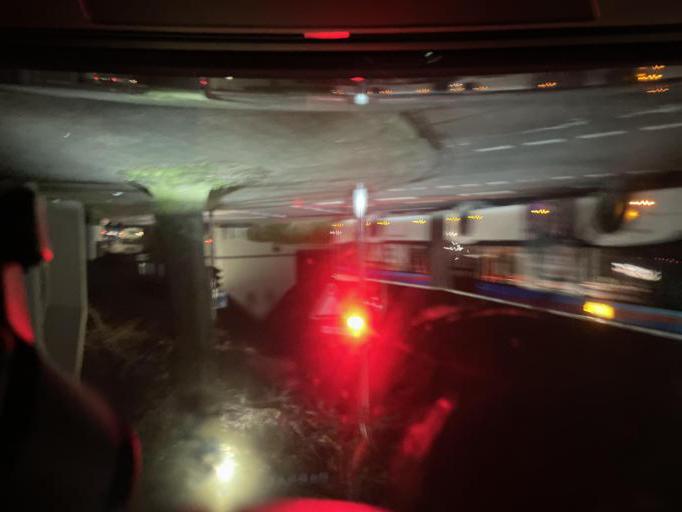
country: DE
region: North Rhine-Westphalia
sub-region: Regierungsbezirk Dusseldorf
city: Monchengladbach
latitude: 51.2194
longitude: 6.4698
